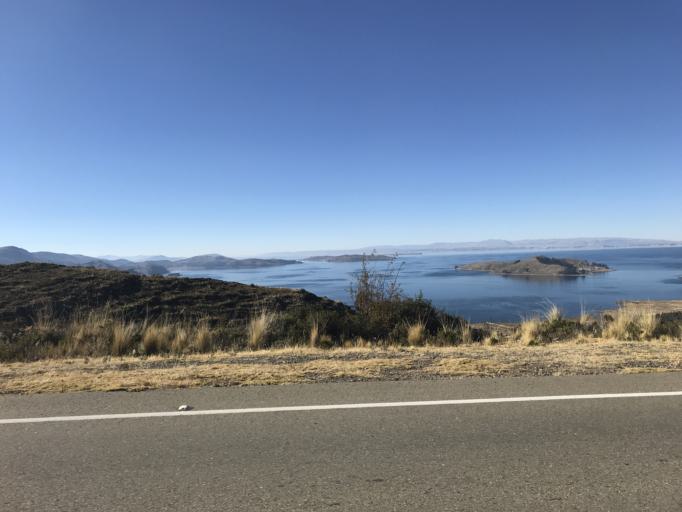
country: BO
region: La Paz
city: San Pedro
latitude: -16.1874
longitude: -68.9667
